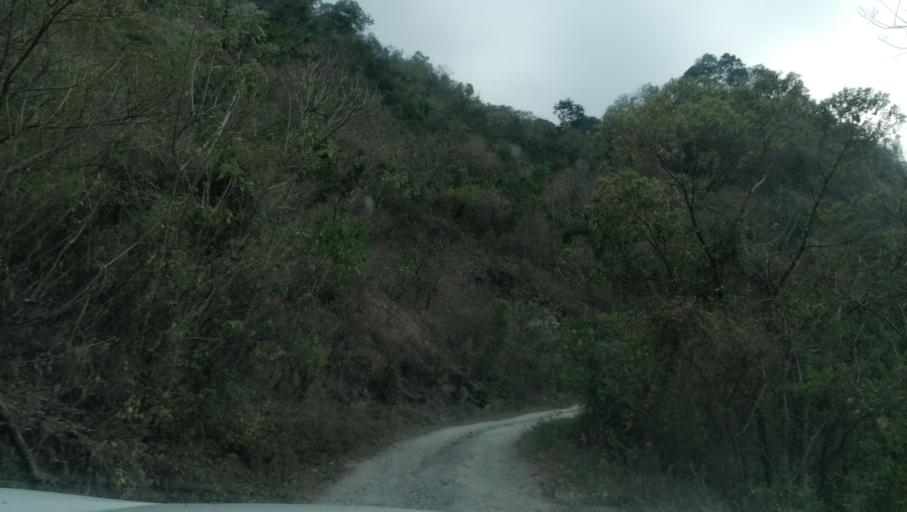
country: MX
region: Chiapas
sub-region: Cacahoatan
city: Benito Juarez
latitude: 15.1619
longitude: -92.1774
